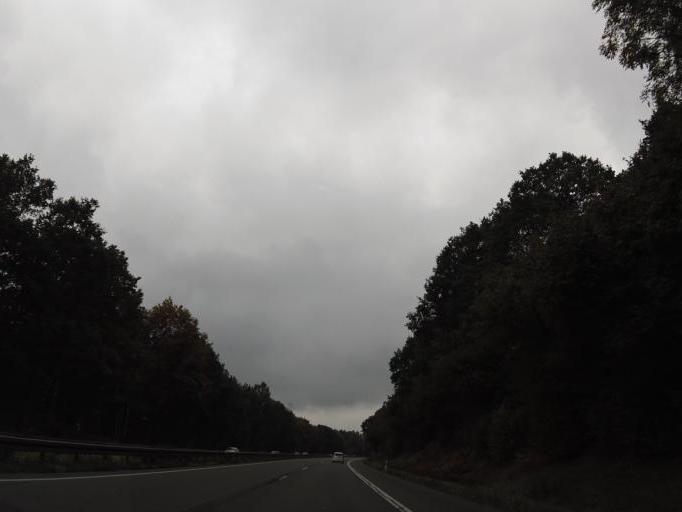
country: DE
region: Saarland
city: Kirkel
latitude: 49.3039
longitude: 7.2469
